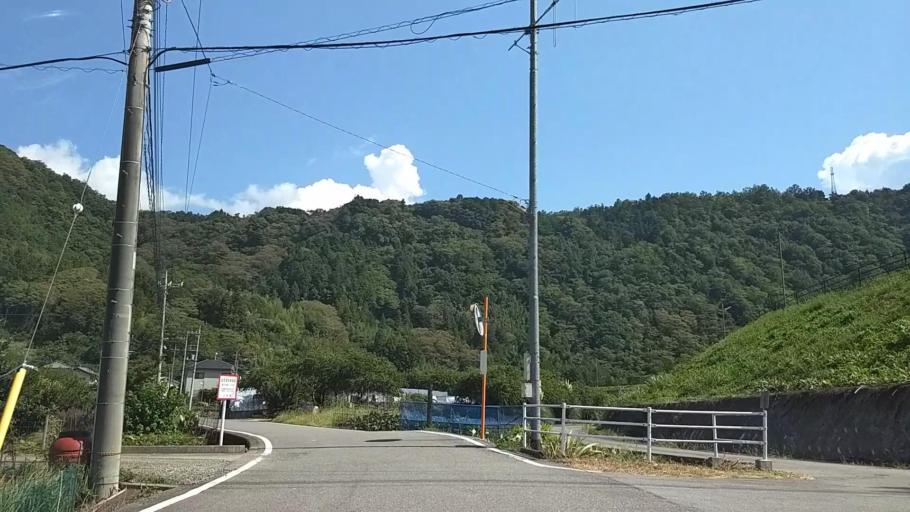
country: JP
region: Yamanashi
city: Ryuo
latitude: 35.5133
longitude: 138.4602
